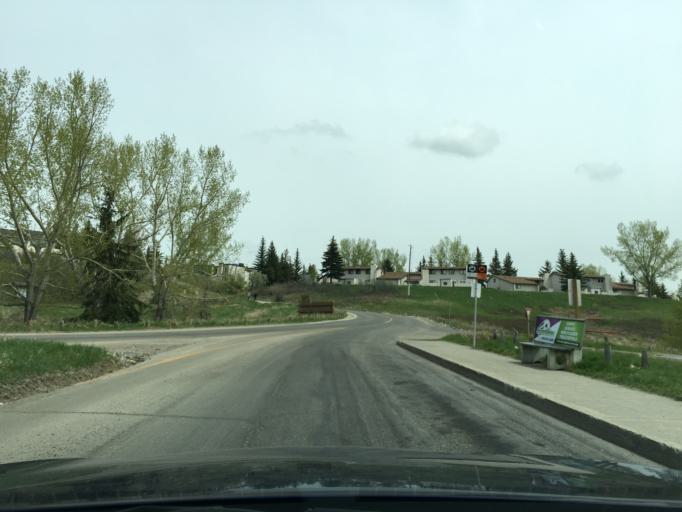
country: CA
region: Alberta
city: Calgary
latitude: 50.9339
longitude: -114.0848
